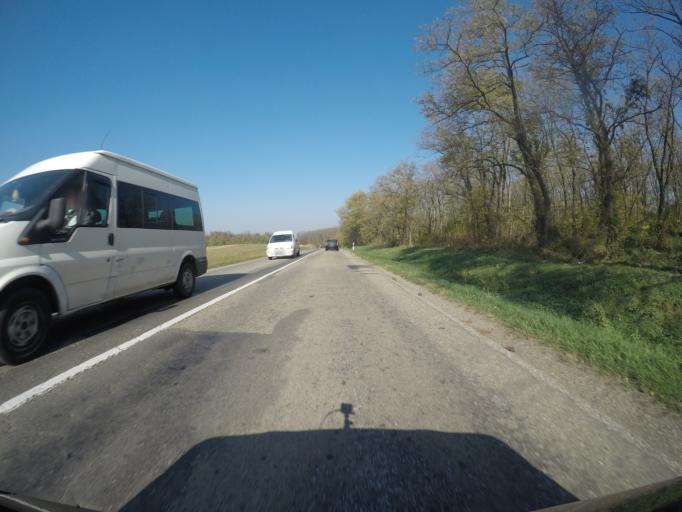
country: HU
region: Tolna
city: Szedres
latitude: 46.4625
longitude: 18.6887
